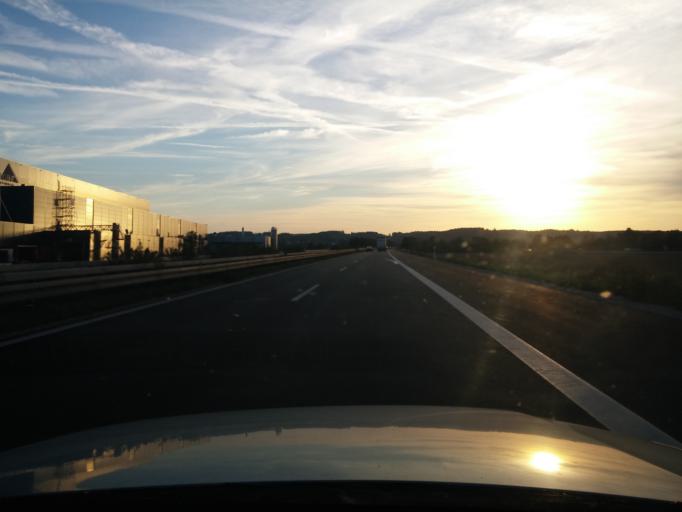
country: DE
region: Bavaria
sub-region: Swabia
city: Bad Worishofen
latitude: 48.0412
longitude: 10.5961
